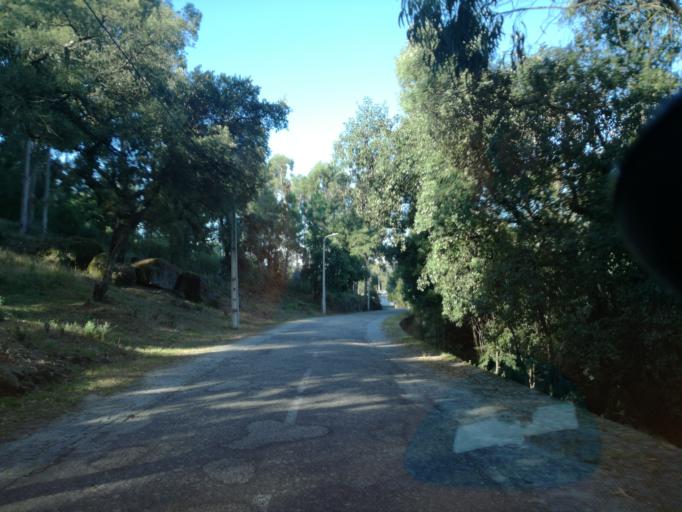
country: PT
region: Porto
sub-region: Pacos de Ferreira
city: Seroa
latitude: 41.2909
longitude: -8.4247
